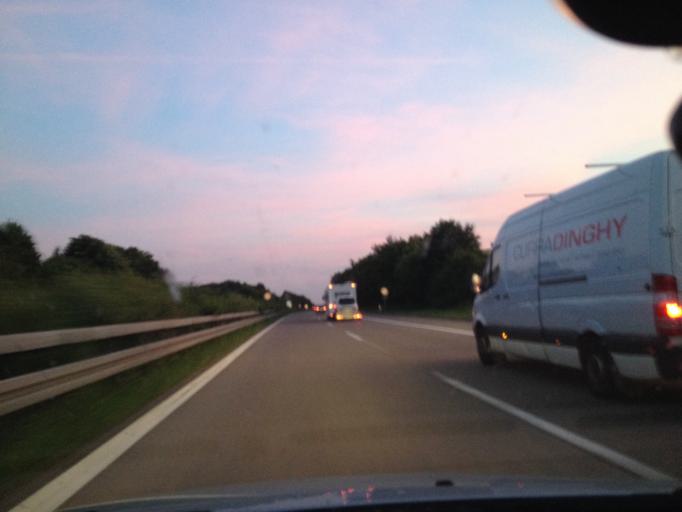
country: DE
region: Baden-Wuerttemberg
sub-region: Regierungsbezirk Stuttgart
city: Herbrechtingen
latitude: 48.5861
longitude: 10.1799
